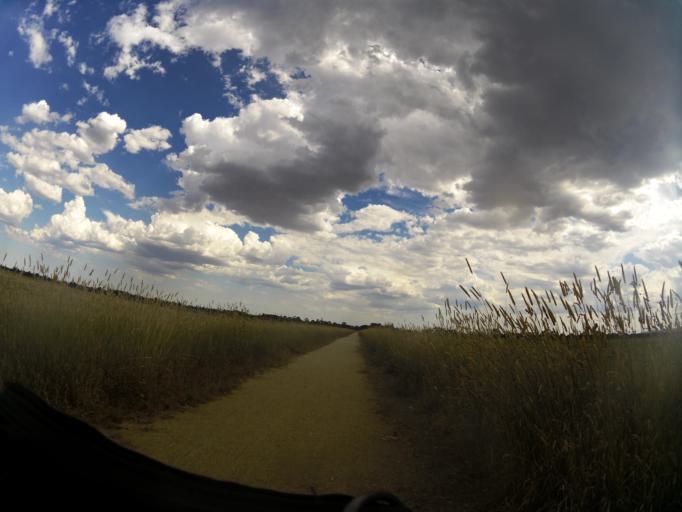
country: AU
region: Victoria
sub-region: Wellington
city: Heyfield
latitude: -38.0010
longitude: 146.6980
